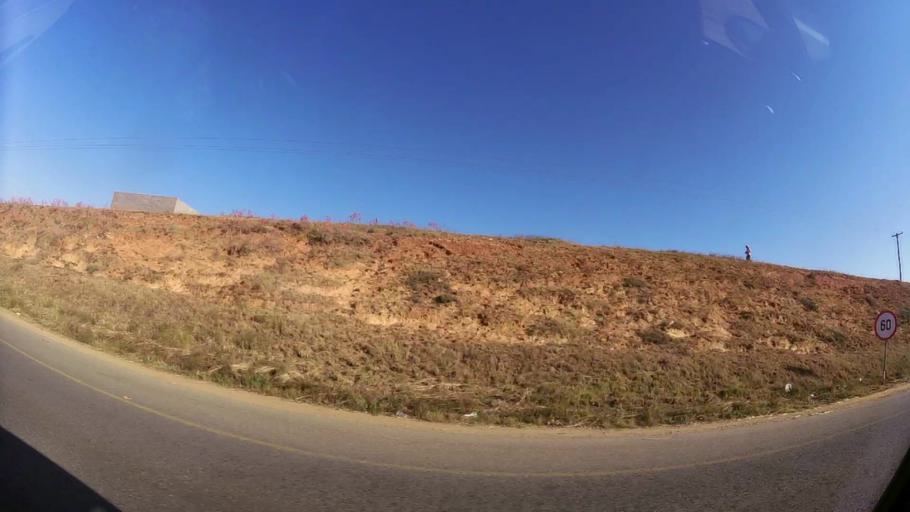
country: ZA
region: Gauteng
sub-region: City of Johannesburg Metropolitan Municipality
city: Midrand
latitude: -25.9039
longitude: 28.1021
